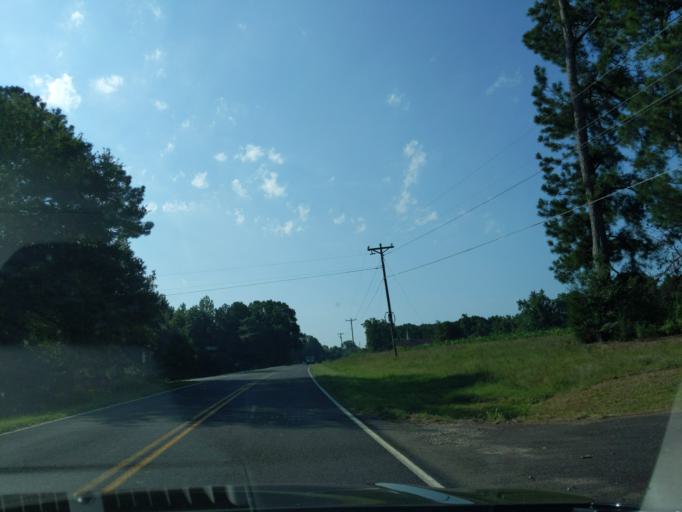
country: US
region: South Carolina
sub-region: Lexington County
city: Leesville
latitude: 34.0206
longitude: -81.5229
